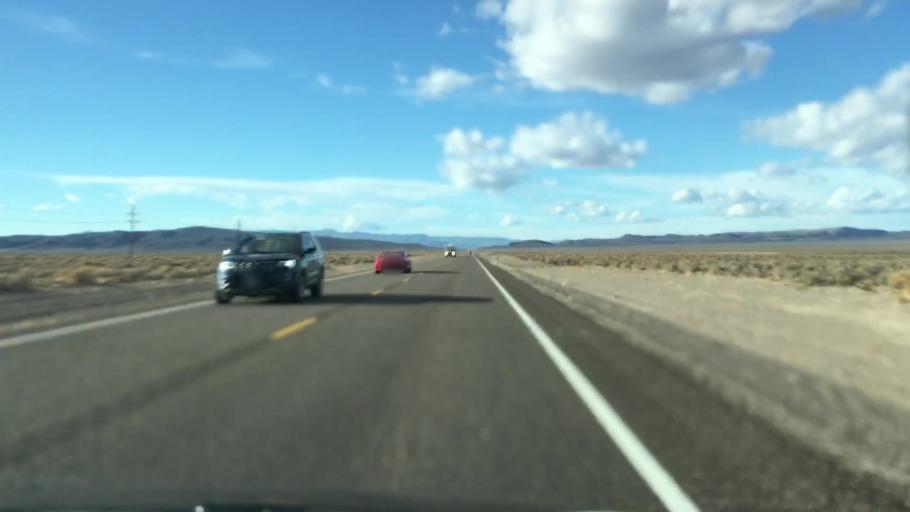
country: US
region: Nevada
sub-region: Nye County
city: Beatty
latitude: 37.1330
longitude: -116.8458
